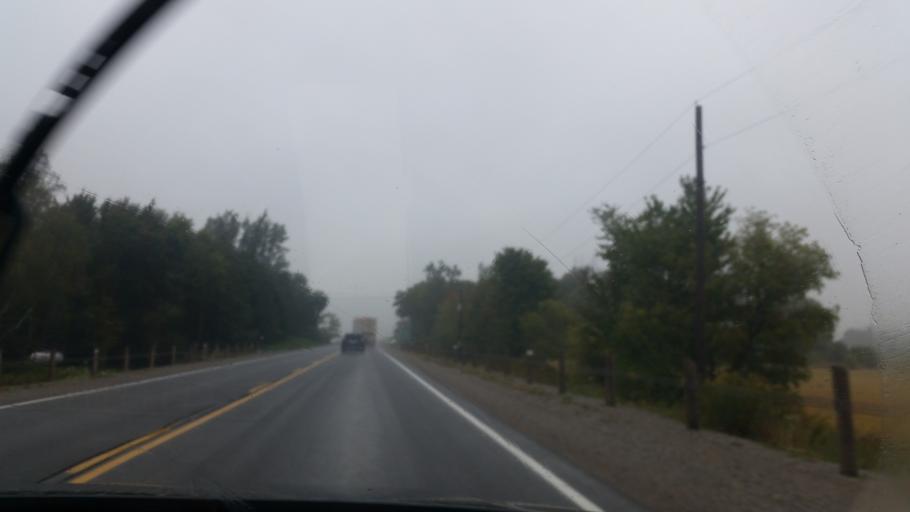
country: CA
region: Ontario
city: London
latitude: 43.2008
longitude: -81.2332
